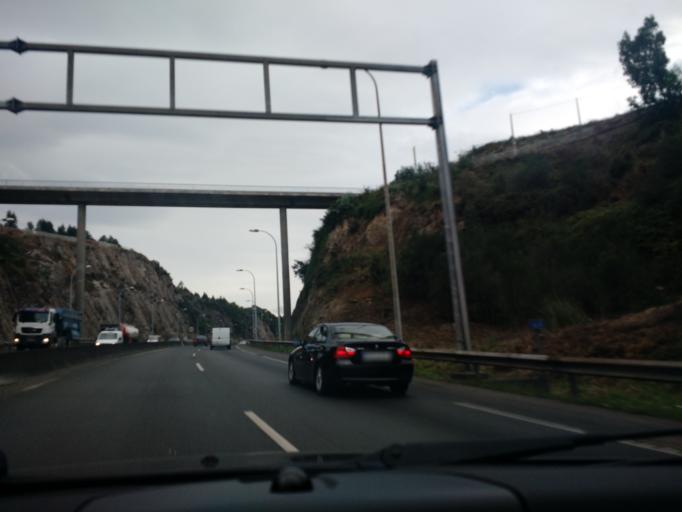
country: ES
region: Galicia
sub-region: Provincia da Coruna
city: Culleredo
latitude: 43.3255
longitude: -8.3942
